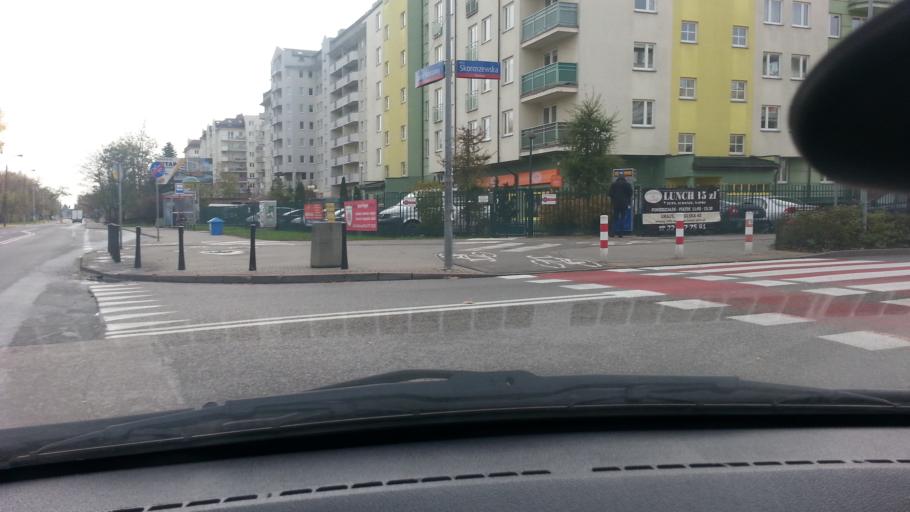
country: PL
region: Masovian Voivodeship
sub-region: Warszawa
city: Ursus
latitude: 52.1938
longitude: 20.9030
